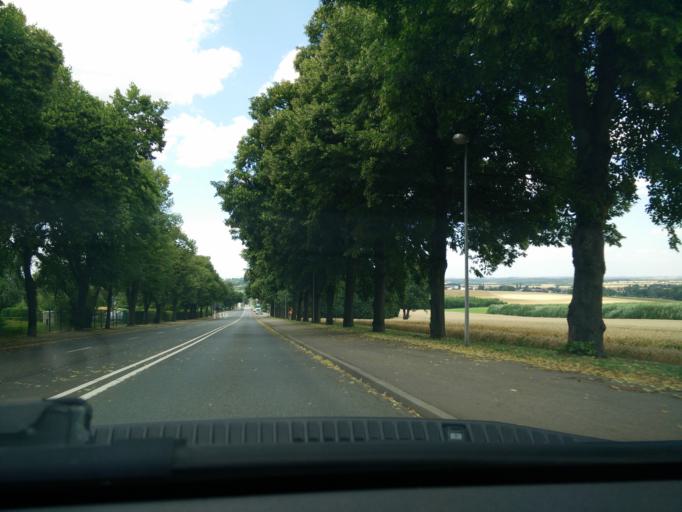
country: DE
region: Saxony
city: Hartmannsdorf
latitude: 50.8825
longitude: 12.8128
